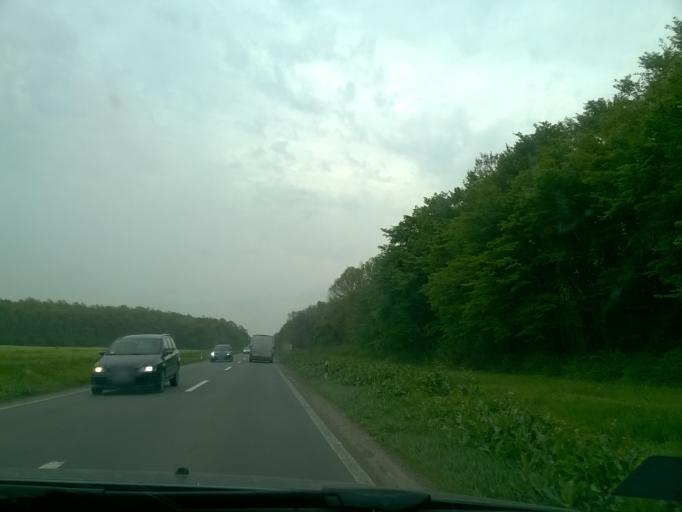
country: RS
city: Platicevo
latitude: 44.8404
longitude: 19.7693
